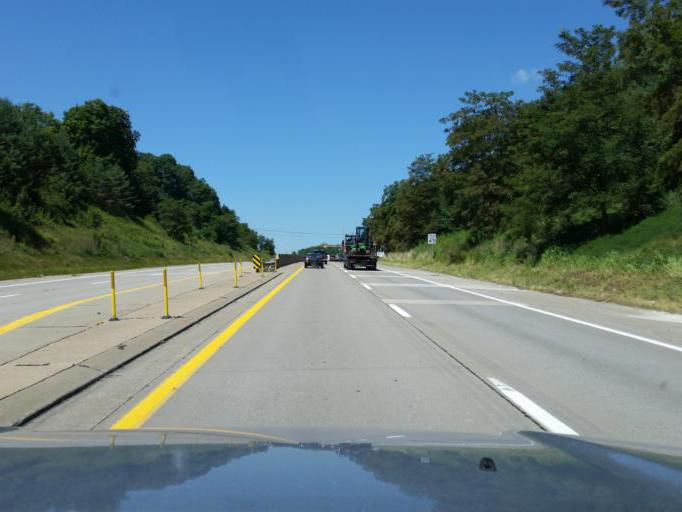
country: US
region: Pennsylvania
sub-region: Westmoreland County
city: Delmont
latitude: 40.4019
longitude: -79.5162
